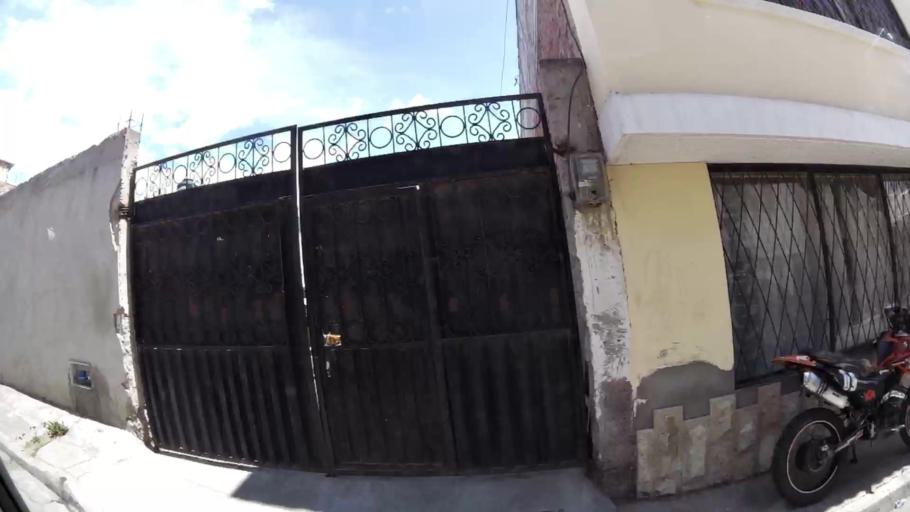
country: EC
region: Chimborazo
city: Riobamba
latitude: -1.6609
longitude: -78.6427
